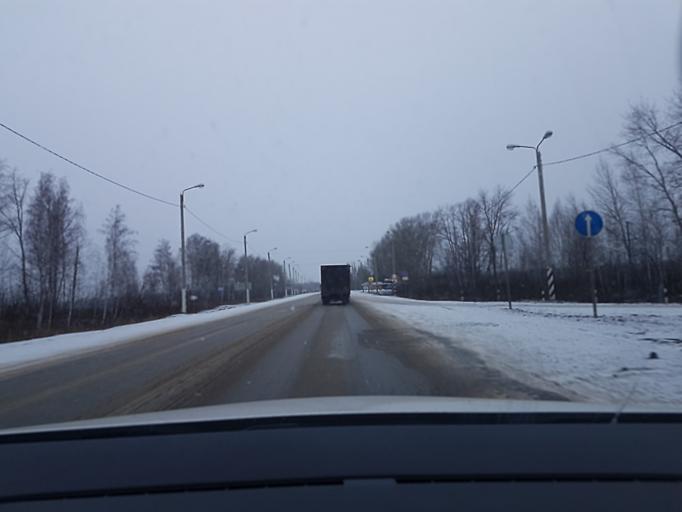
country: RU
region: Tambov
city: Pervomayskiy
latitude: 53.2457
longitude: 40.2537
